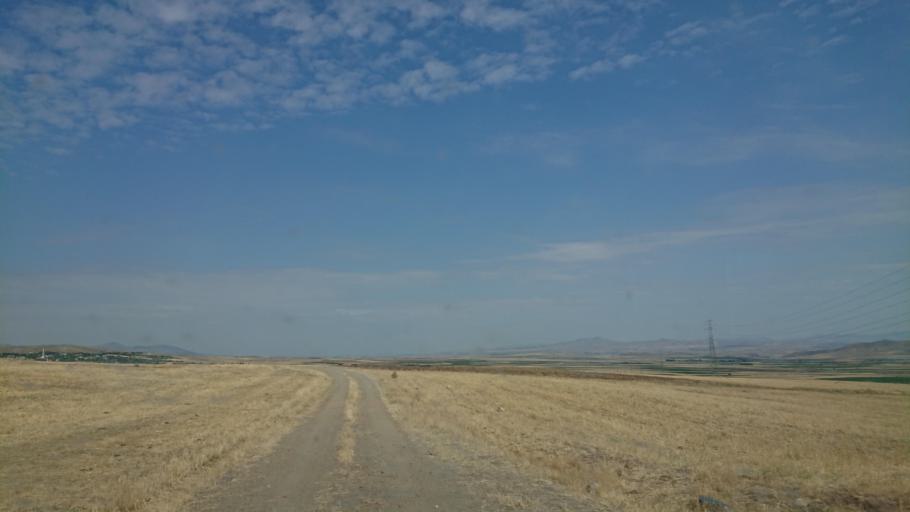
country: TR
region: Aksaray
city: Sariyahsi
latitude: 38.9517
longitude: 33.9106
